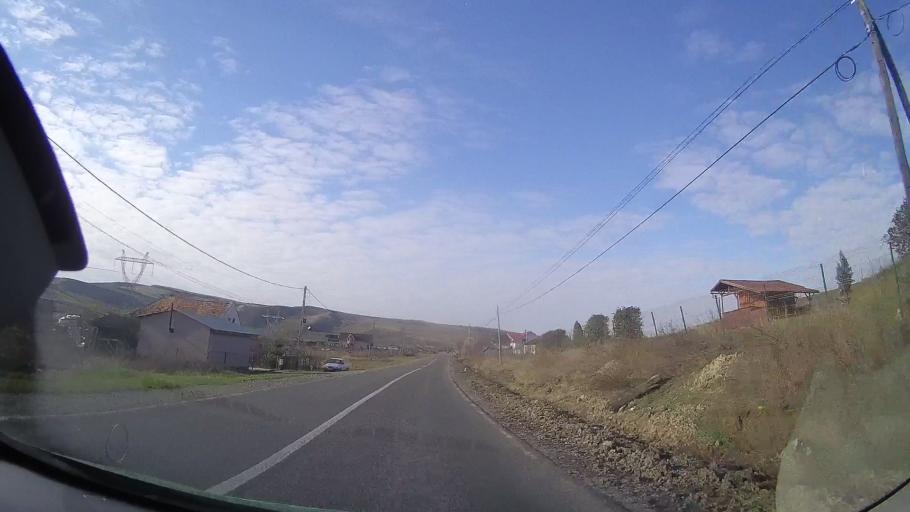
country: RO
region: Cluj
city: Caianu Mic
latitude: 46.7971
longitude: 23.8827
